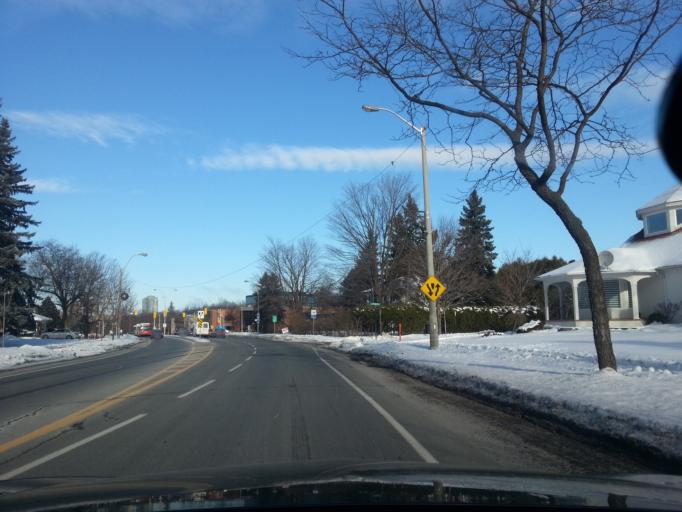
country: CA
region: Ontario
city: Ottawa
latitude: 45.3971
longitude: -75.6618
